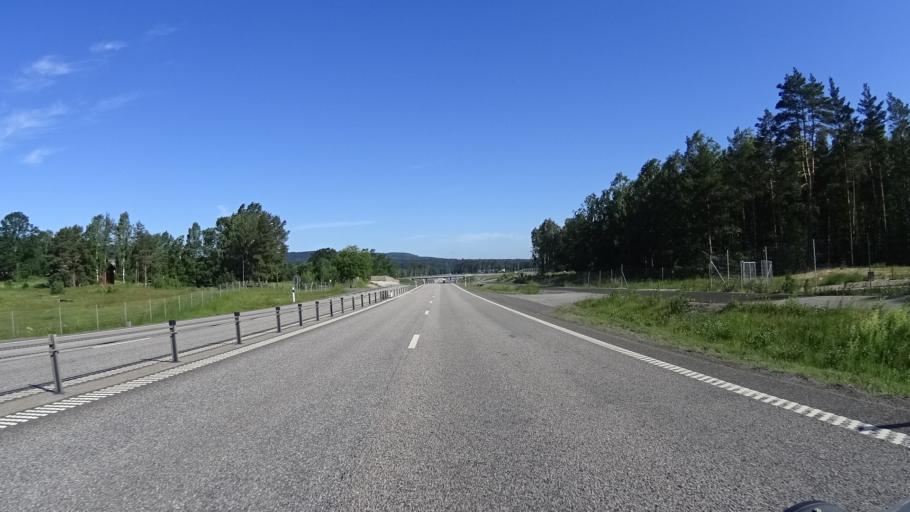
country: SE
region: Vaestra Goetaland
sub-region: Skovde Kommun
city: Stopen
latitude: 58.4325
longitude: 13.8613
